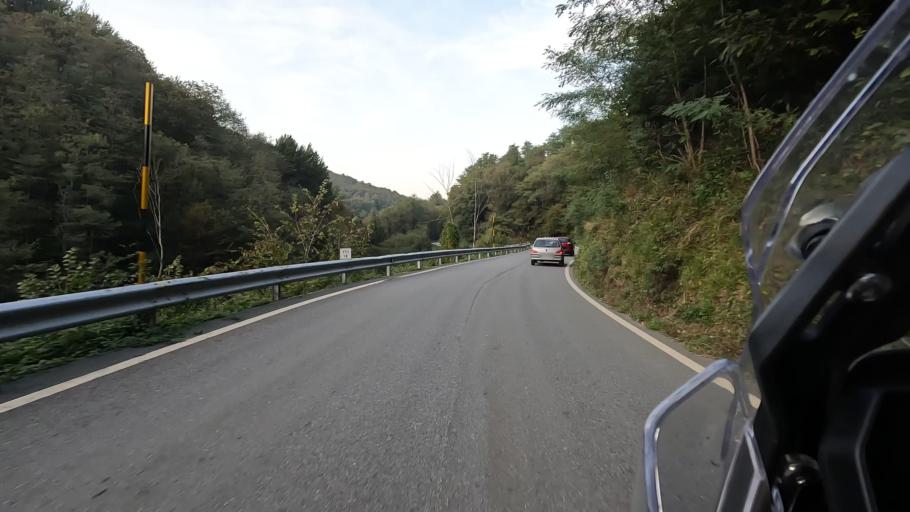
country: IT
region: Liguria
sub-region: Provincia di Savona
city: Osteria dei Cacciatori-Stella
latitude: 44.4545
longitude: 8.4798
